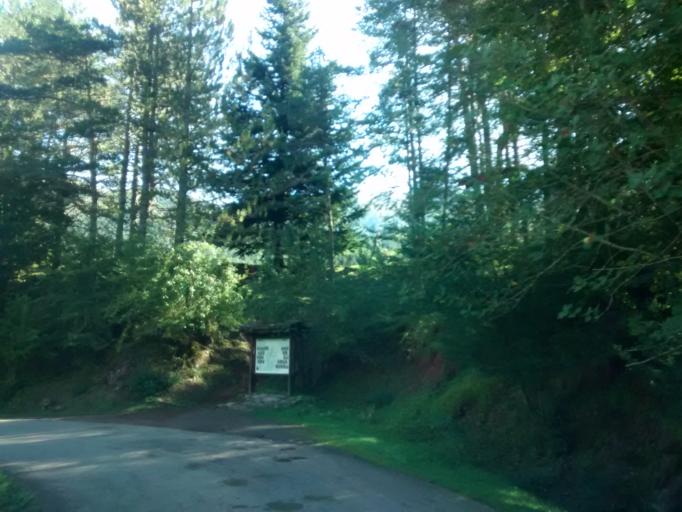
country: ES
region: Aragon
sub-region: Provincia de Huesca
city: Aragues del Puerto
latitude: 42.8319
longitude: -0.7111
